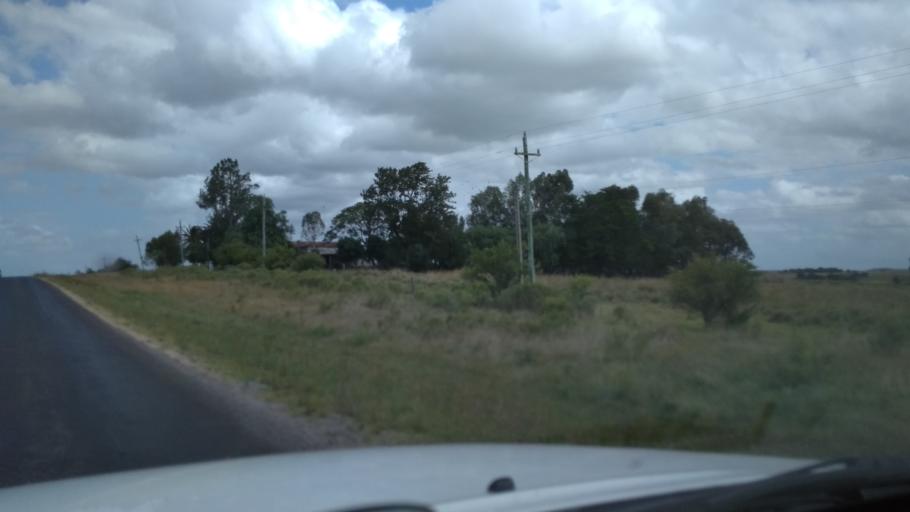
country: UY
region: Canelones
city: San Ramon
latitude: -34.1972
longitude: -55.9360
